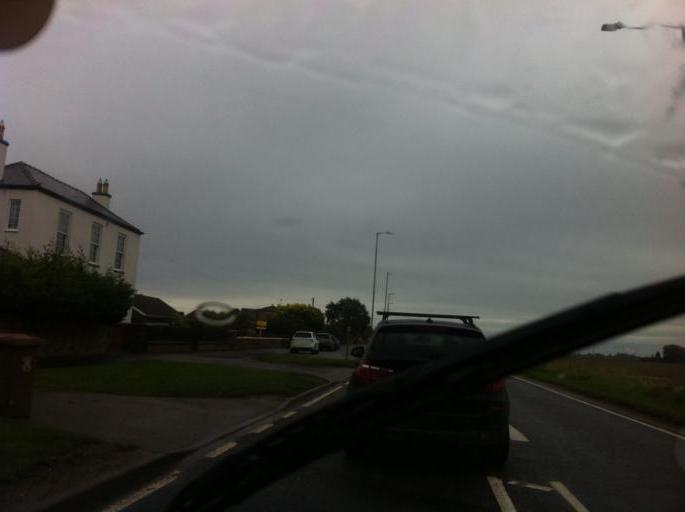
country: GB
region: England
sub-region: Lincolnshire
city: Boston
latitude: 52.9874
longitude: 0.0013
